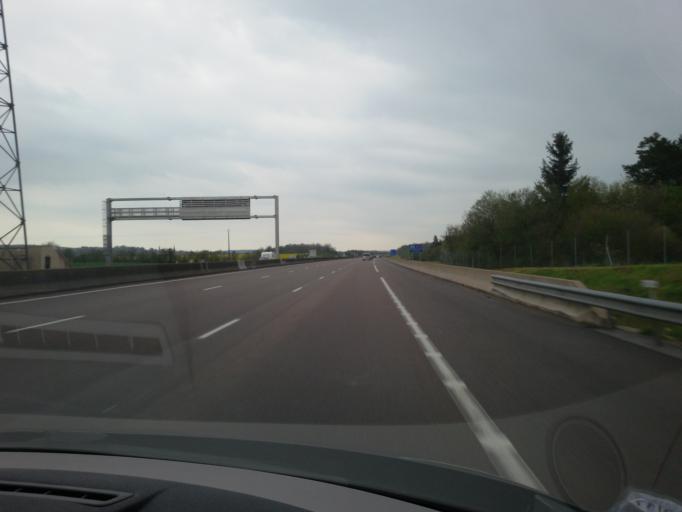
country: FR
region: Champagne-Ardenne
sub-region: Departement de la Haute-Marne
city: Langres
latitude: 47.8211
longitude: 5.2250
